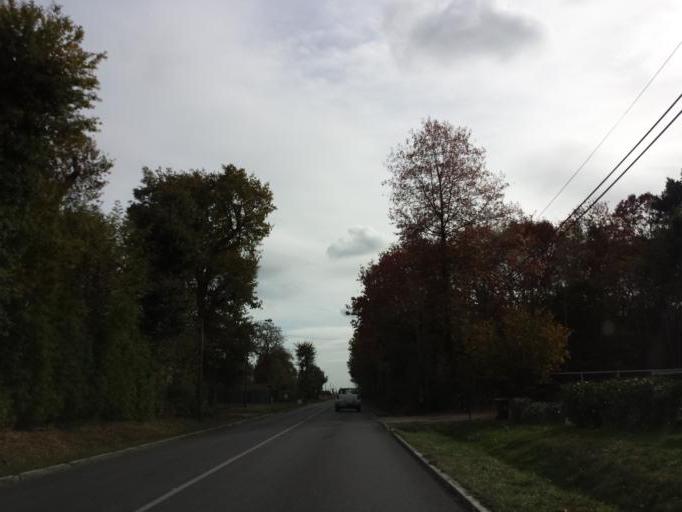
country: FR
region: Aquitaine
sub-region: Departement de la Gironde
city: Marcheprime
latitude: 44.7774
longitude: -0.9303
